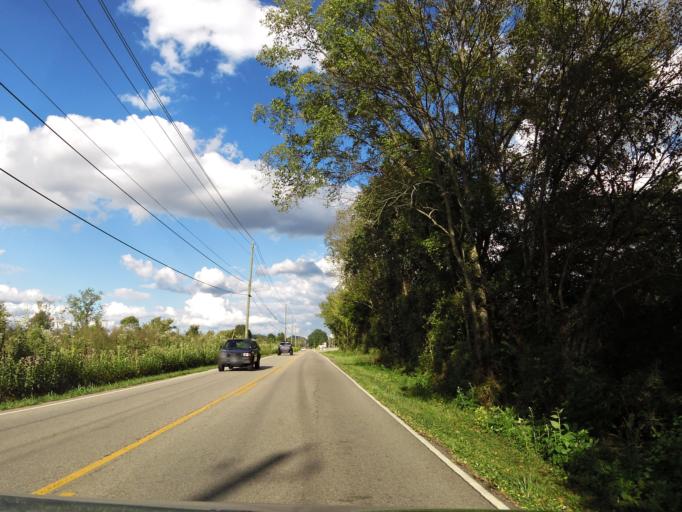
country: US
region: Tennessee
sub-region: Knox County
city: Knoxville
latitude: 36.0601
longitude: -83.8635
